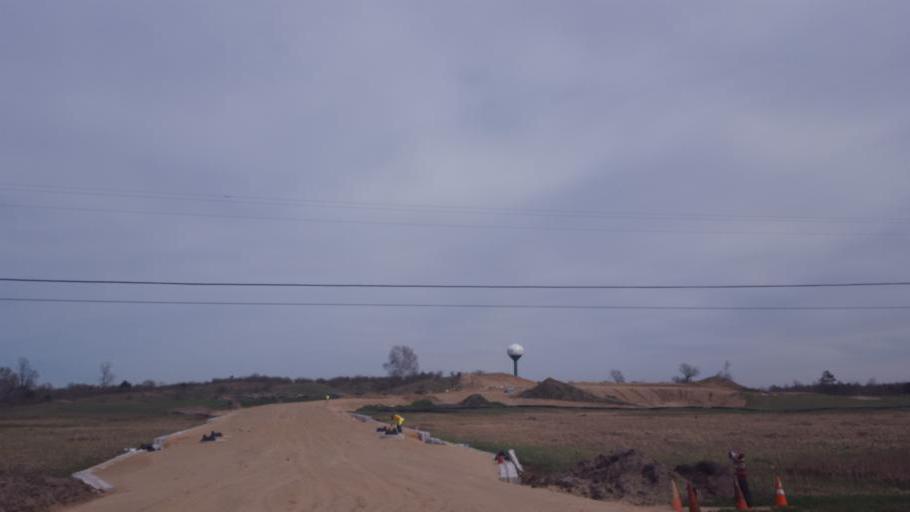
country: US
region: Michigan
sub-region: Clare County
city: Clare
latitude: 43.8492
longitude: -84.7681
